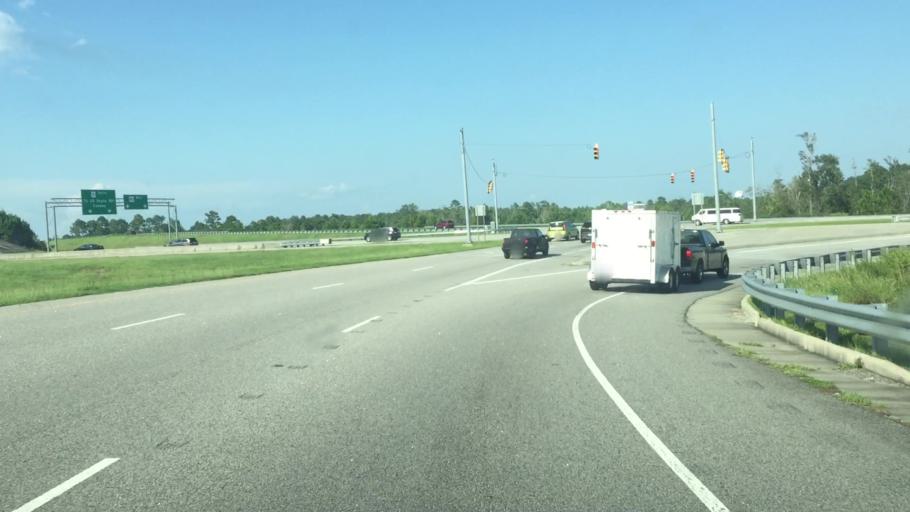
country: US
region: South Carolina
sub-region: Horry County
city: North Myrtle Beach
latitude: 33.8424
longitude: -78.7016
